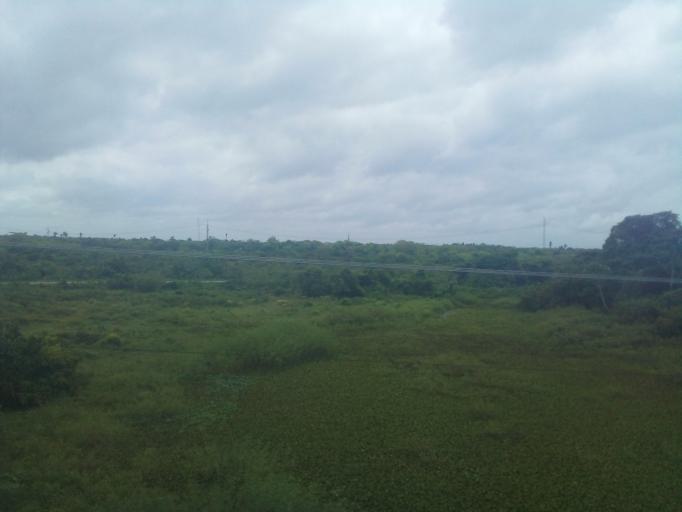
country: BR
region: Maranhao
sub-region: Arari
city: Arari
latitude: -3.5758
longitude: -44.7445
